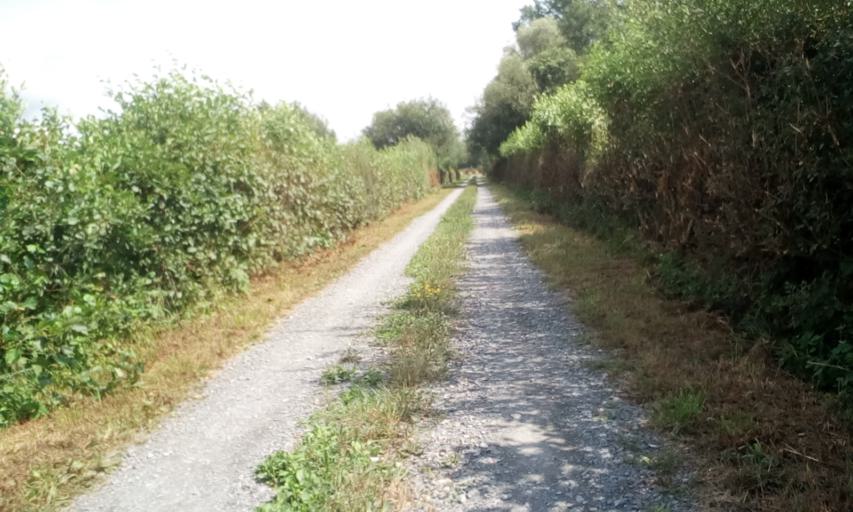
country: FR
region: Lower Normandy
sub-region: Departement du Calvados
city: Bavent
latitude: 49.2386
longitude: -0.1651
